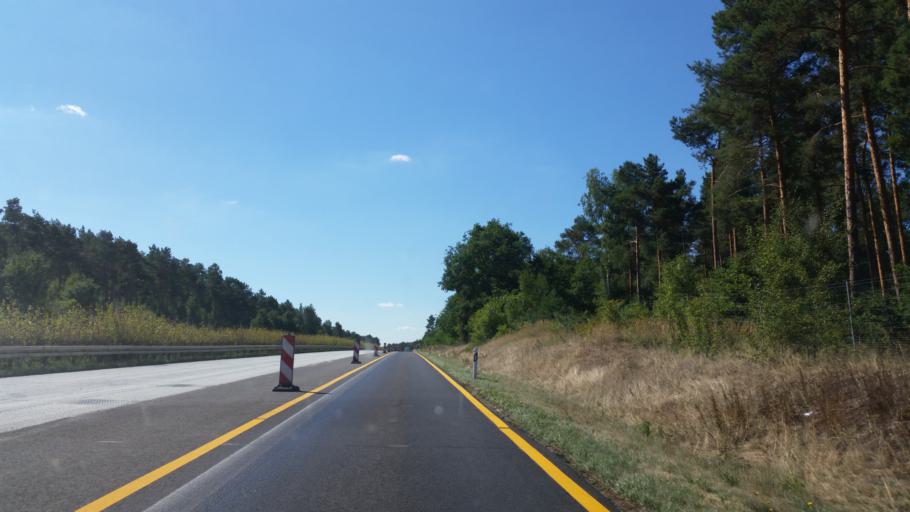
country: DE
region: Brandenburg
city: Teupitz
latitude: 52.0875
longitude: 13.6485
